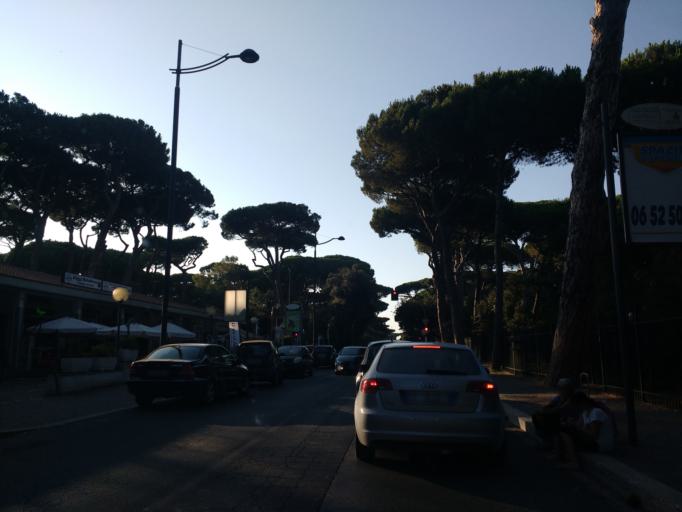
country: IT
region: Latium
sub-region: Citta metropolitana di Roma Capitale
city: Fregene
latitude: 41.8552
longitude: 12.1985
